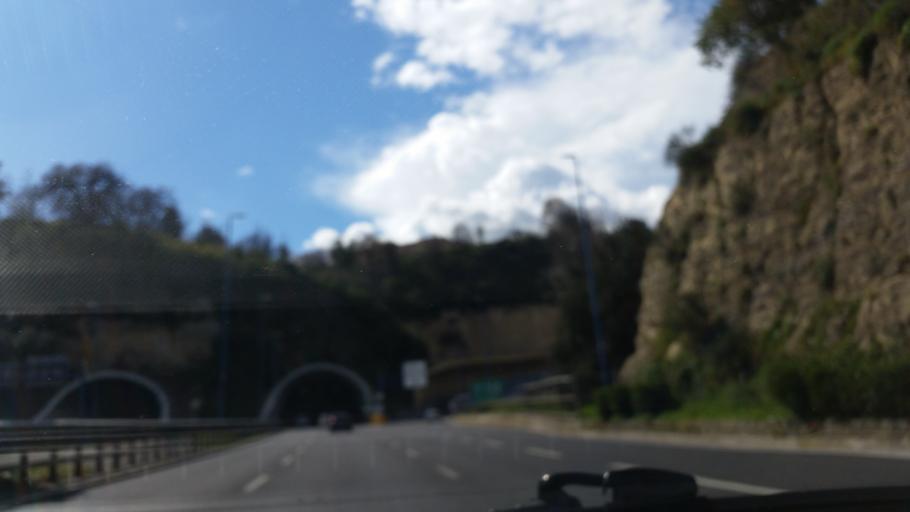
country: IT
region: Campania
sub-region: Provincia di Napoli
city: Napoli
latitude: 40.8620
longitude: 14.2337
